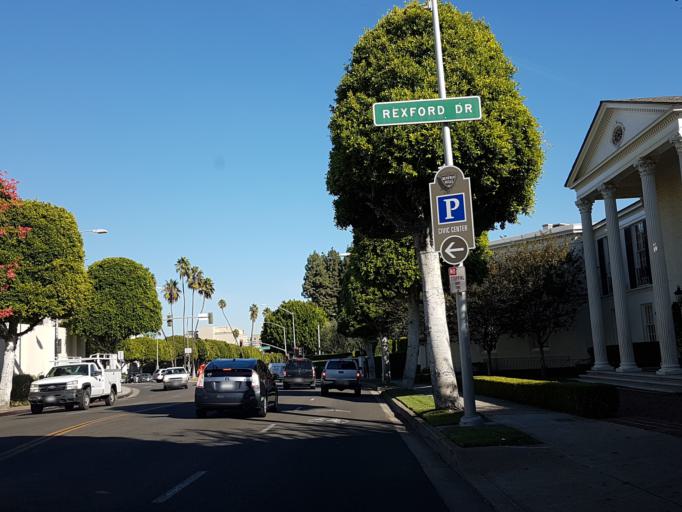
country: US
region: California
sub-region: Los Angeles County
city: Beverly Hills
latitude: 34.0719
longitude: -118.4000
